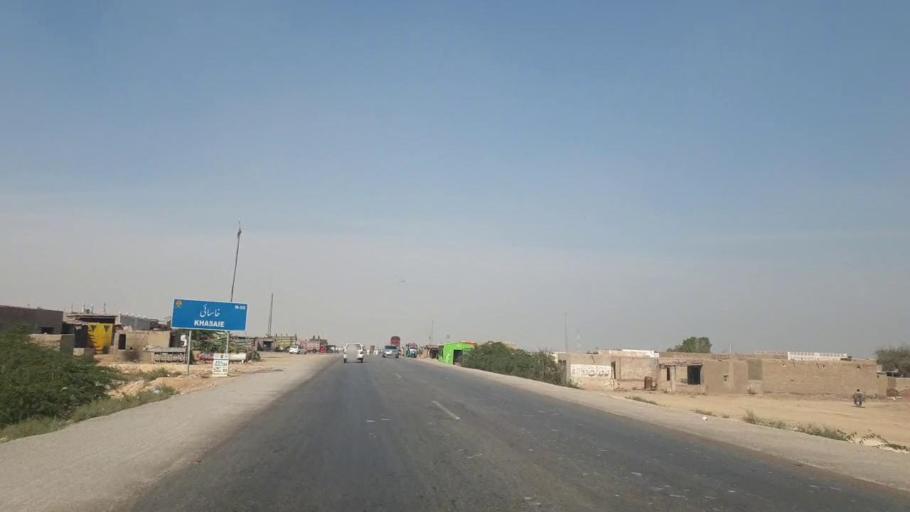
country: PK
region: Sindh
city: Hala
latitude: 25.7920
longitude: 68.2811
